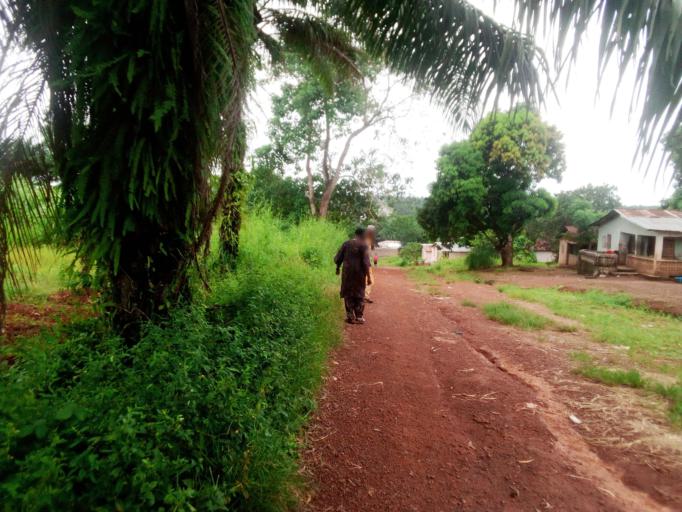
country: SL
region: Northern Province
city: Kambia
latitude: 9.1140
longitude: -12.9289
